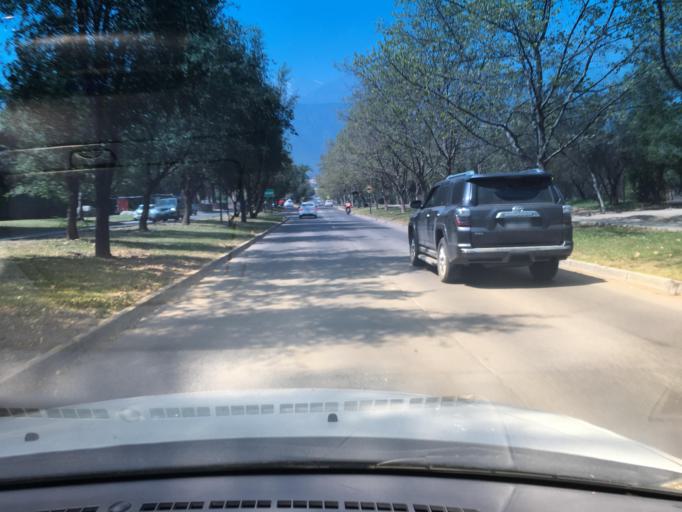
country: CL
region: Santiago Metropolitan
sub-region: Provincia de Santiago
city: Villa Presidente Frei, Nunoa, Santiago, Chile
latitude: -33.5134
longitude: -70.5394
